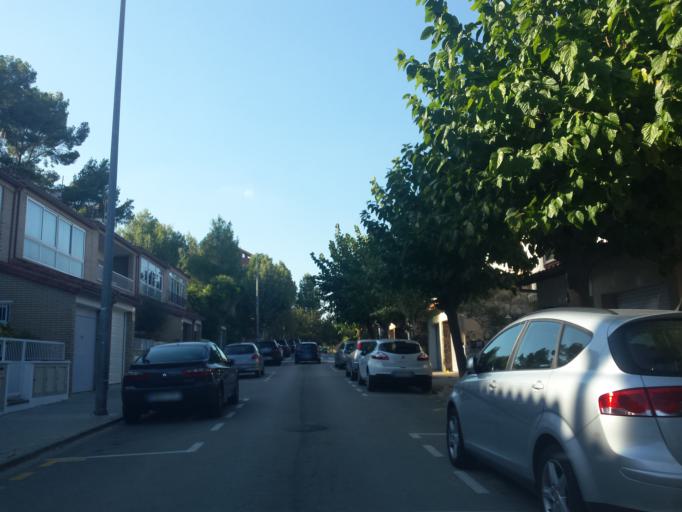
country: ES
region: Catalonia
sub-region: Provincia de Barcelona
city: Sant Andreu de la Barca
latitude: 41.4478
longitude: 1.9664
